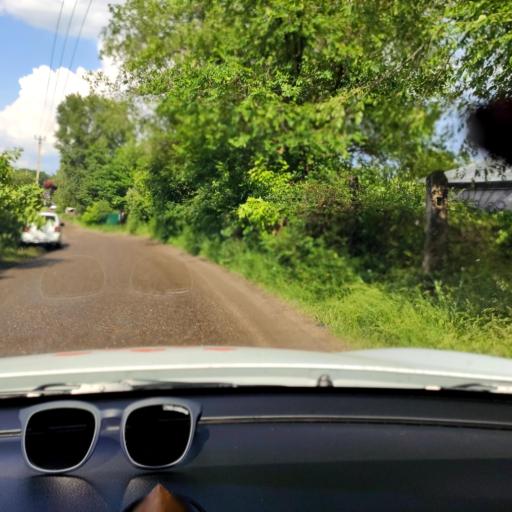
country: RU
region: Tatarstan
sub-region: Zelenodol'skiy Rayon
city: Vasil'yevo
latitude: 55.8277
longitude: 48.7424
